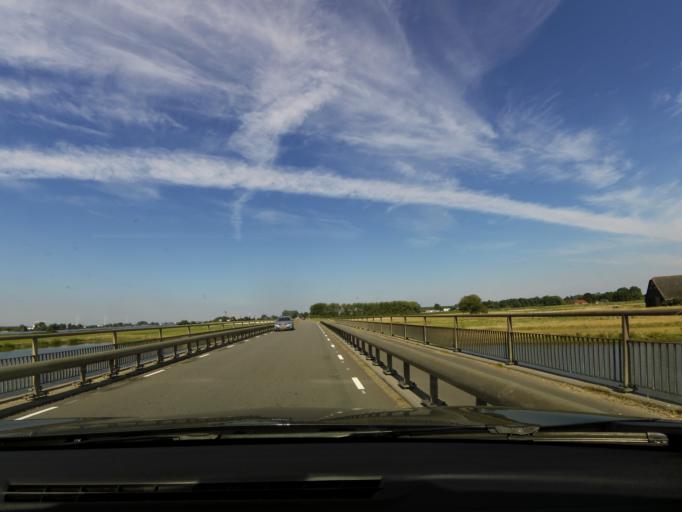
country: NL
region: South Holland
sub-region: Gemeente Hardinxveld-Giessendam
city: Neder-Hardinxveld
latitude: 51.7971
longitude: 4.8586
